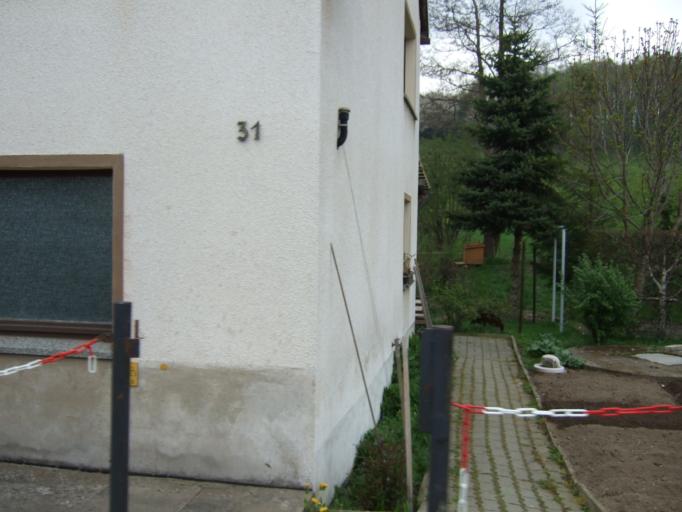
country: DE
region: Saxony
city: Grosshartmannsdorf
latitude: 50.8102
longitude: 13.3728
